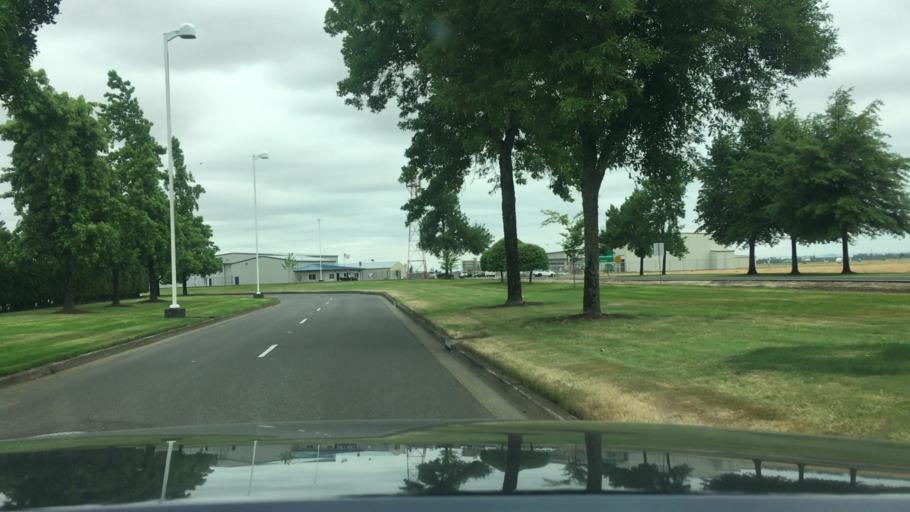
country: US
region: Oregon
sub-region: Lane County
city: Junction City
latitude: 44.1198
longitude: -123.2089
